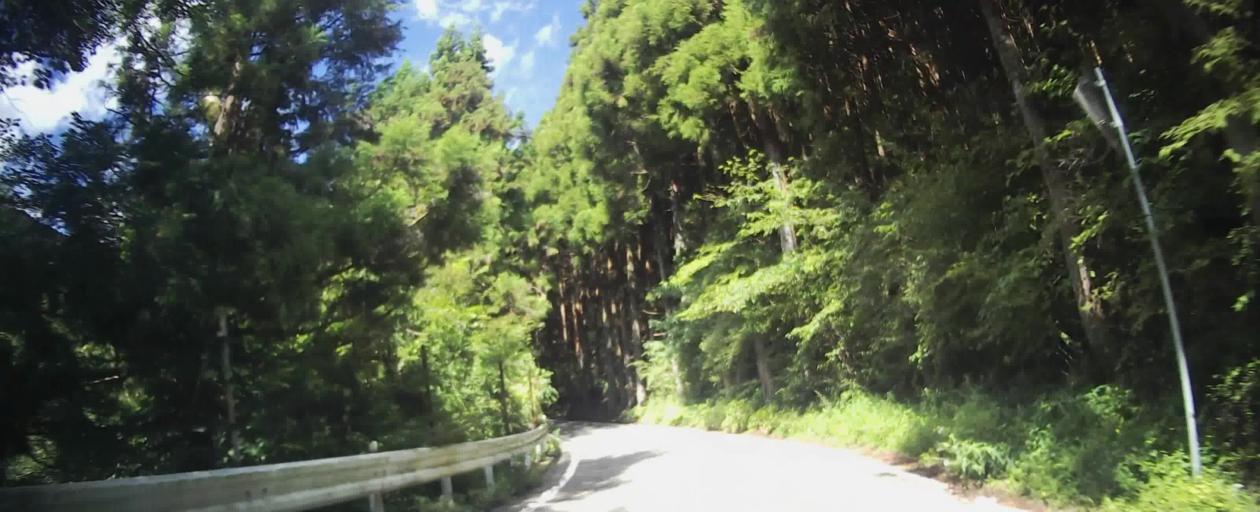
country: JP
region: Gunma
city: Shibukawa
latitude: 36.4557
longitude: 138.8975
